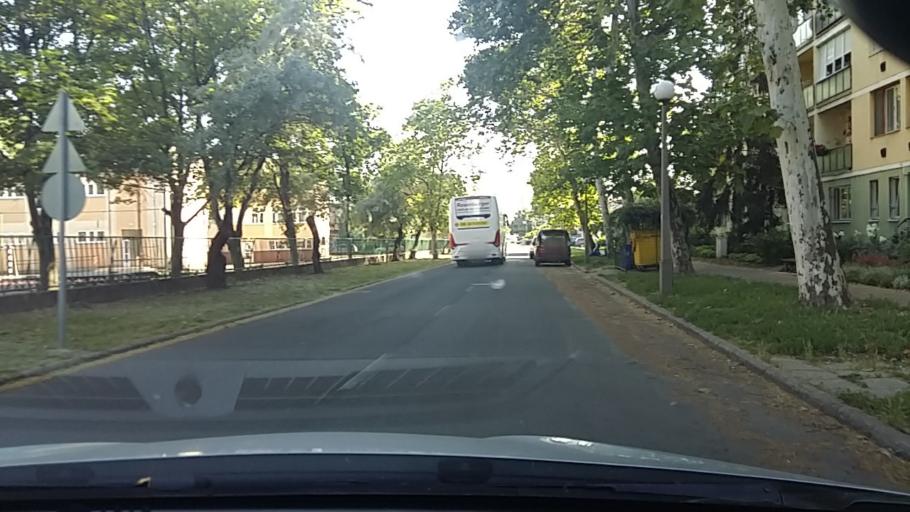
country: HU
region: Heves
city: Gyongyos
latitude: 47.7695
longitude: 19.9225
